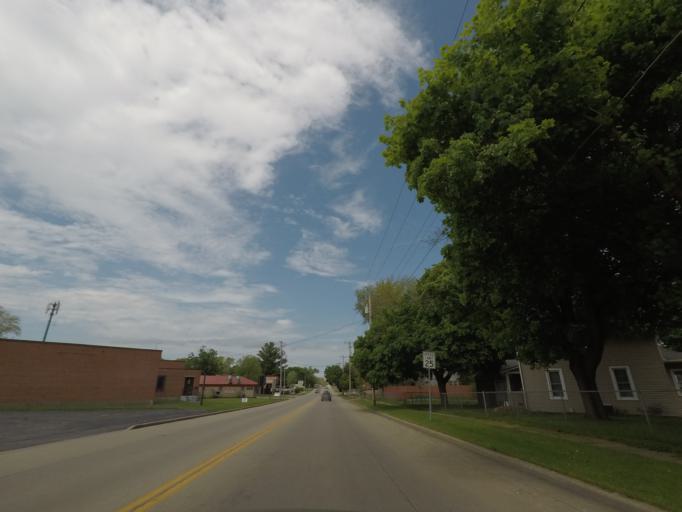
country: US
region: Wisconsin
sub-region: Rock County
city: Beloit
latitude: 42.5115
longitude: -89.0566
